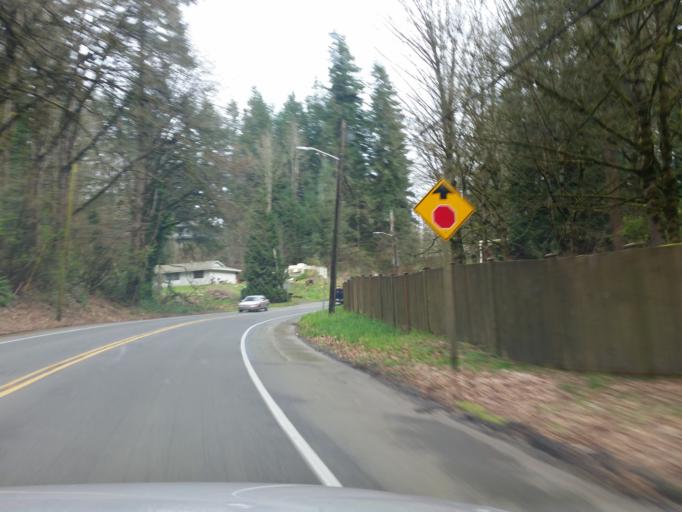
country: US
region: Washington
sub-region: King County
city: Woodinville
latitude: 47.7532
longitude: -122.1419
